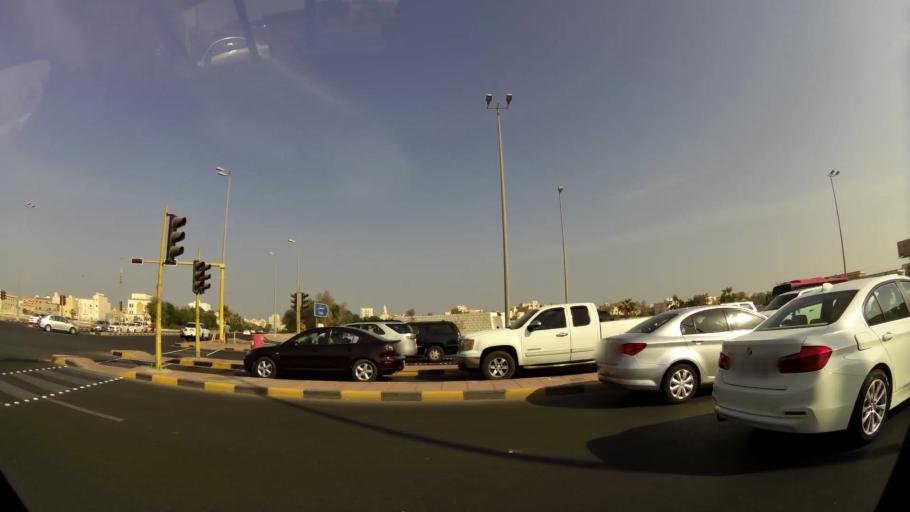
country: KW
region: Mubarak al Kabir
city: Mubarak al Kabir
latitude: 29.1757
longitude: 48.0996
